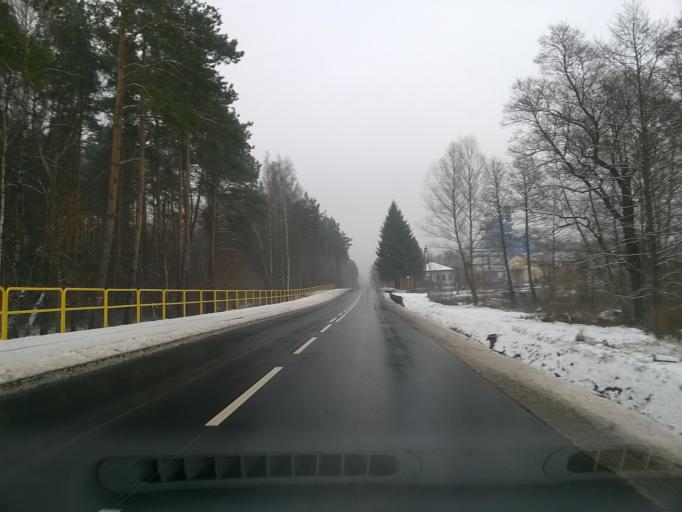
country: PL
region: Kujawsko-Pomorskie
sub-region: Powiat swiecki
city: Swiecie
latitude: 53.4185
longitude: 18.3866
